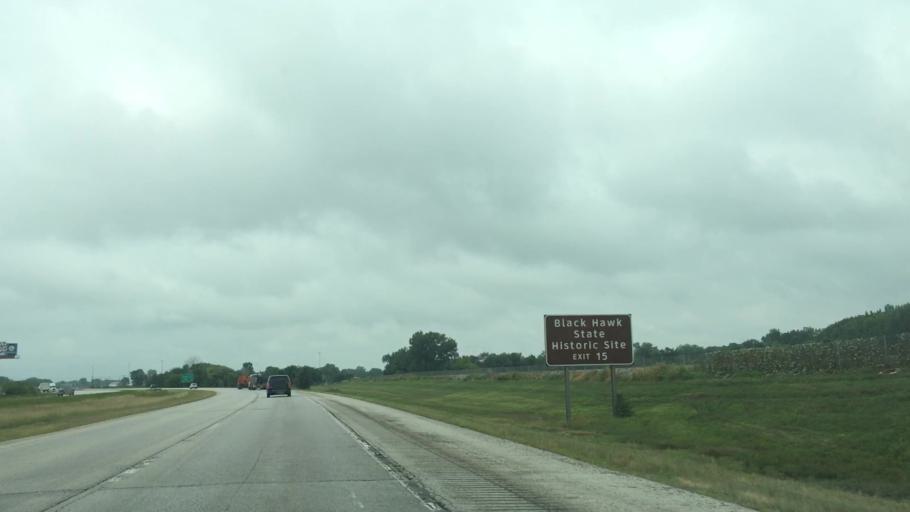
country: US
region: Illinois
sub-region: Rock Island County
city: Milan
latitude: 41.4564
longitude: -90.5376
